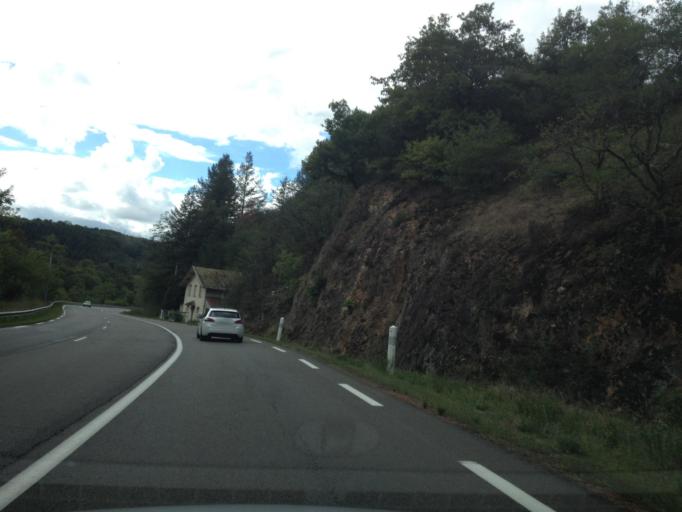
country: FR
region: Rhone-Alpes
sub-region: Departement de la Loire
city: Saint-Symphorien-de-Lay
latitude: 45.9666
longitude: 4.1478
